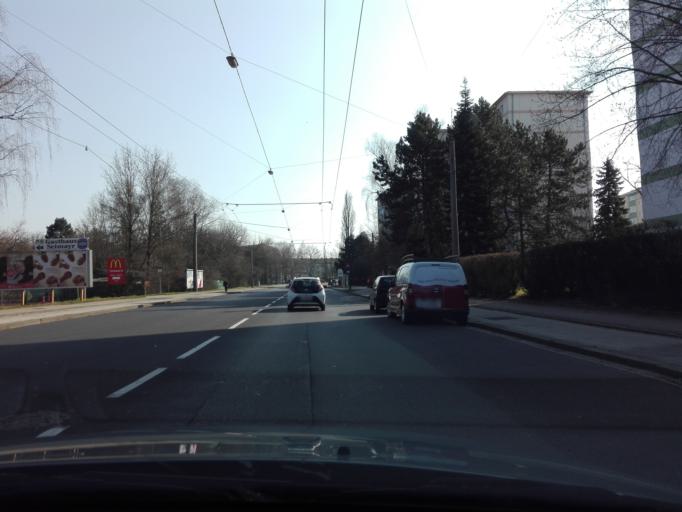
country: AT
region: Upper Austria
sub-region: Politischer Bezirk Linz-Land
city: Leonding
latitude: 48.2607
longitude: 14.2902
